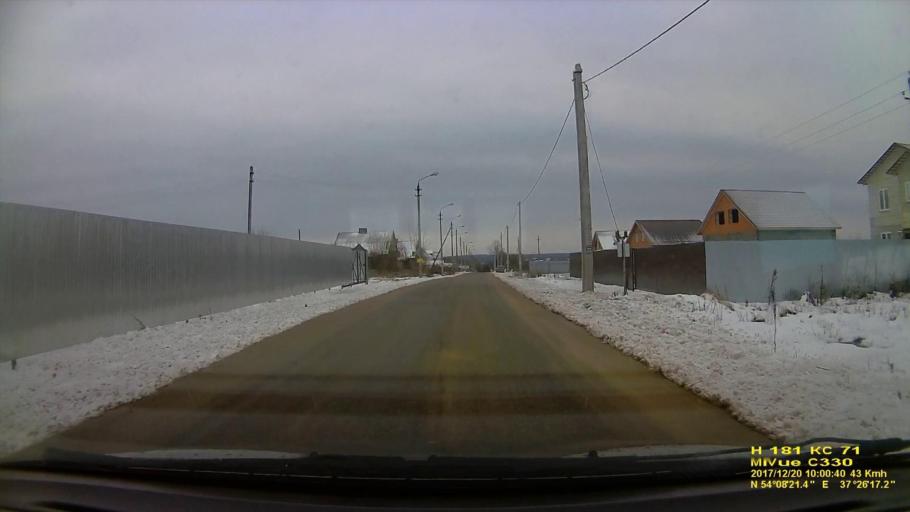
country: RU
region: Tula
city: Kosaya Gora
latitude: 54.1391
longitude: 37.4381
